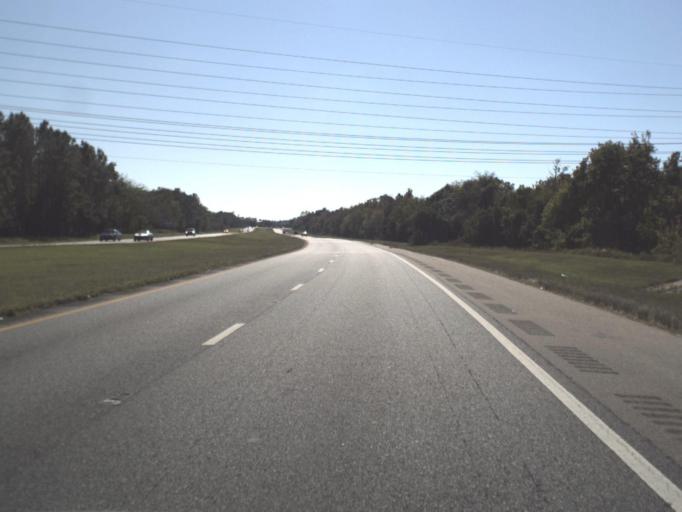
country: US
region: Florida
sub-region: Seminole County
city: Oviedo
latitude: 28.6417
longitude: -81.2409
